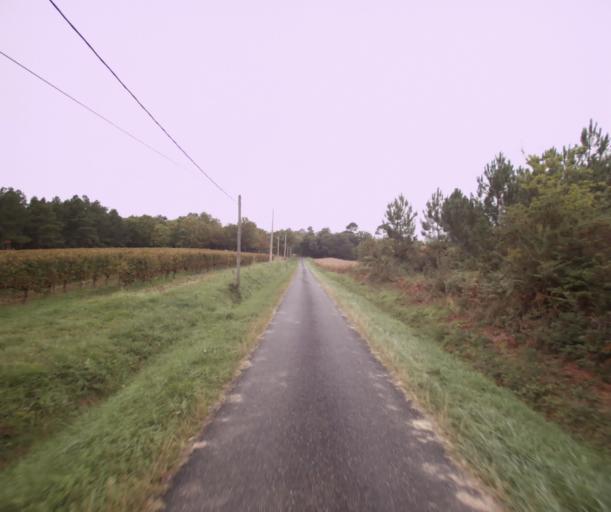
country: FR
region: Midi-Pyrenees
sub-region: Departement du Gers
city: Cazaubon
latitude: 43.8776
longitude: -0.0840
